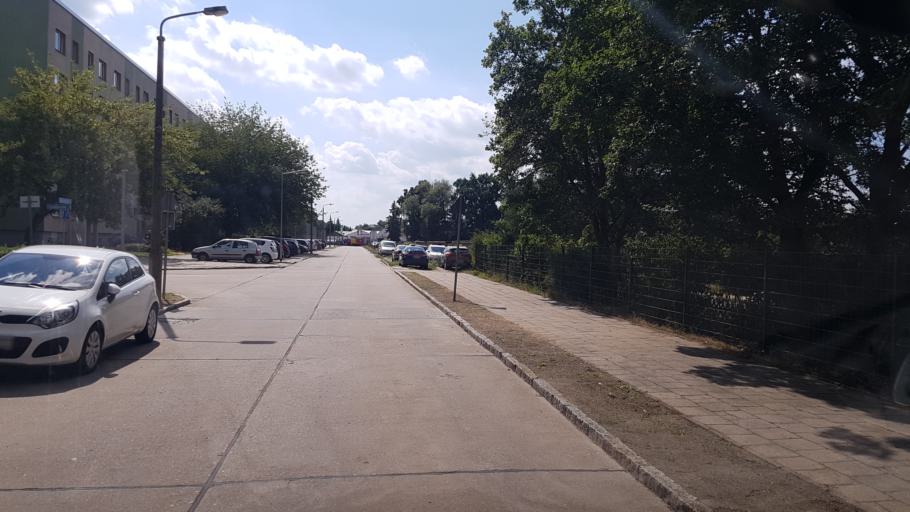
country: DE
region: Brandenburg
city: Lubbenau
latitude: 51.8626
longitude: 13.9371
